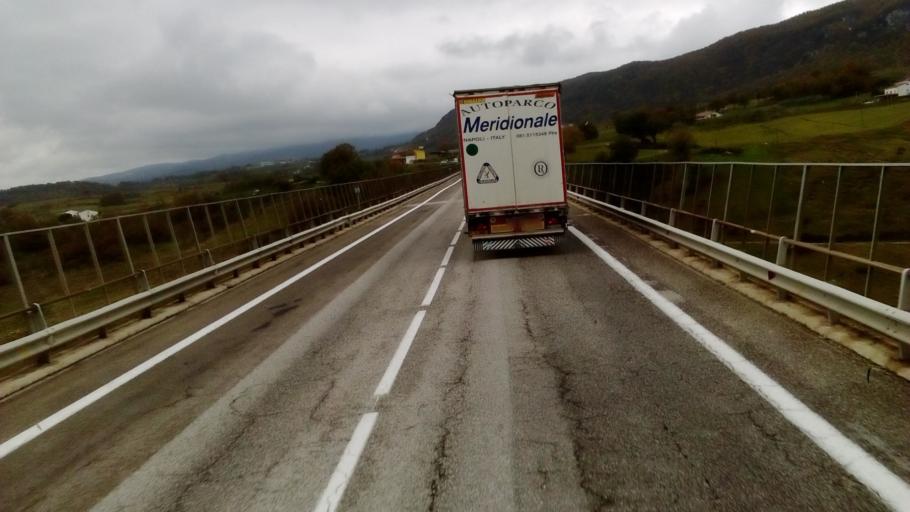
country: IT
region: Molise
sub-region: Provincia di Isernia
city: Civitanova del Sannio
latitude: 41.7038
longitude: 14.4168
